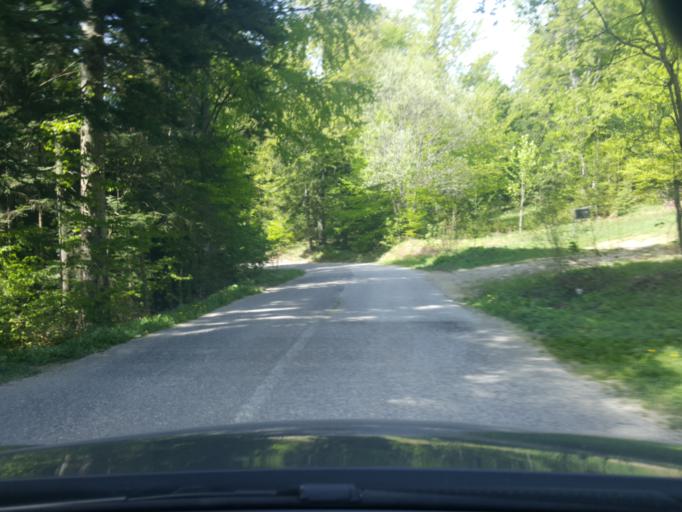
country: RS
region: Central Serbia
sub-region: Zlatiborski Okrug
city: Bajina Basta
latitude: 43.9211
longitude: 19.4843
